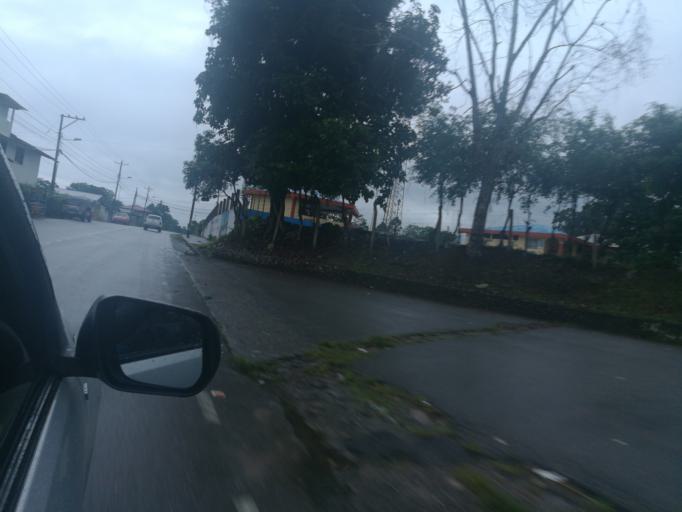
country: EC
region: Napo
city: Tena
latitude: -1.0356
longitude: -77.6686
